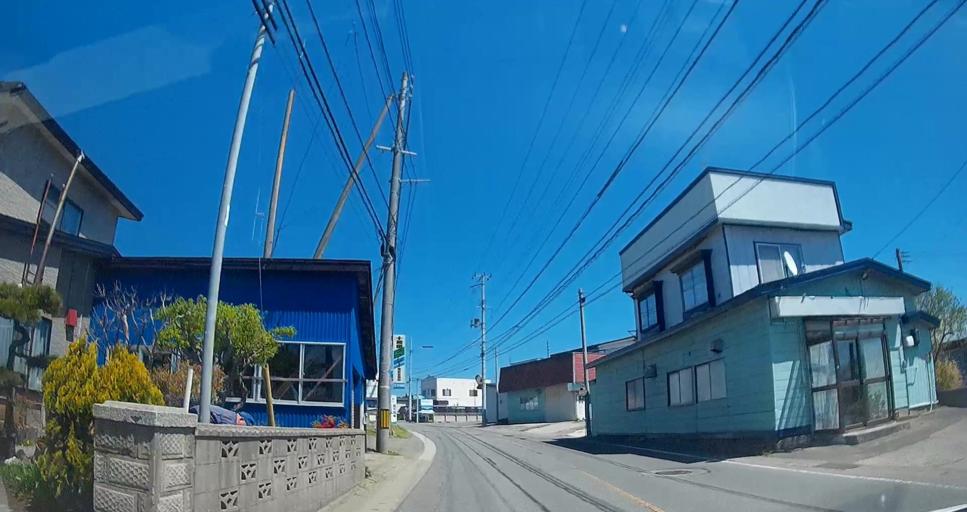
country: JP
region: Aomori
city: Misawa
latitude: 40.9630
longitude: 141.3742
